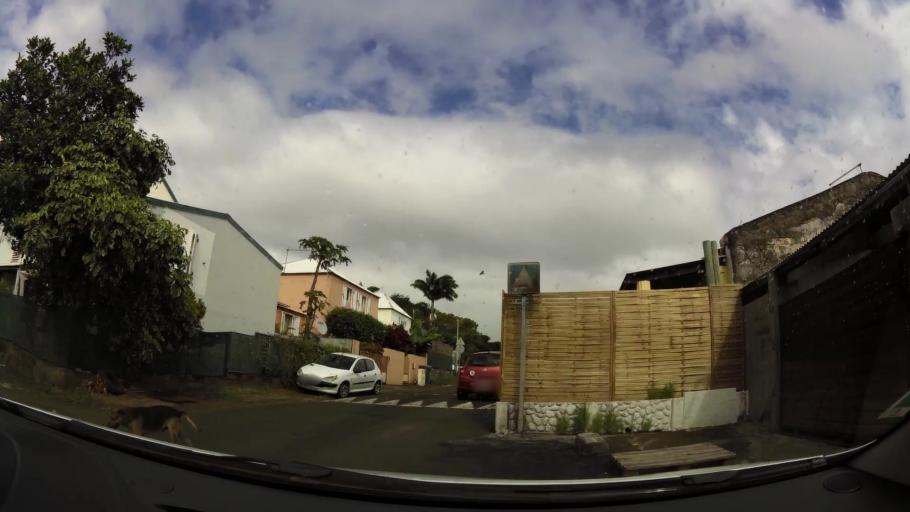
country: RE
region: Reunion
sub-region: Reunion
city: Sainte-Marie
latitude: -20.8952
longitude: 55.5654
